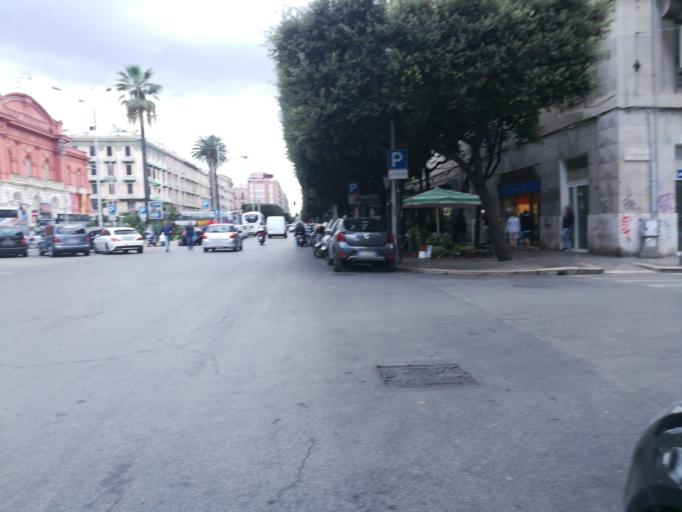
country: IT
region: Apulia
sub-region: Provincia di Bari
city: Bari
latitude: 41.1242
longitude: 16.8722
